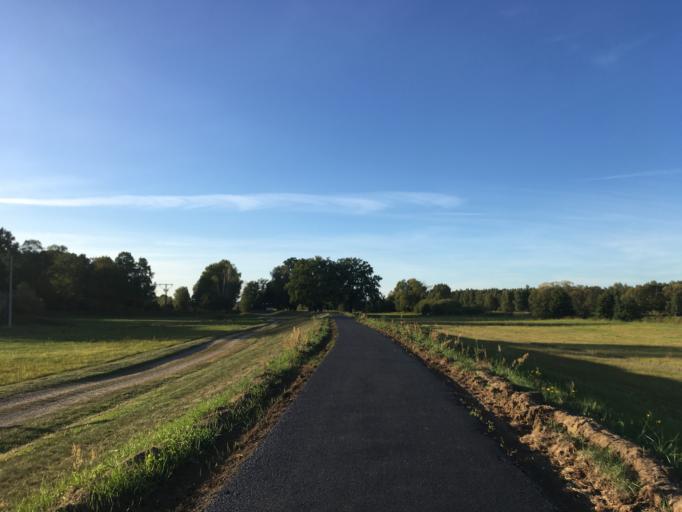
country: DE
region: Brandenburg
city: Forst
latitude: 51.6933
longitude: 14.7185
